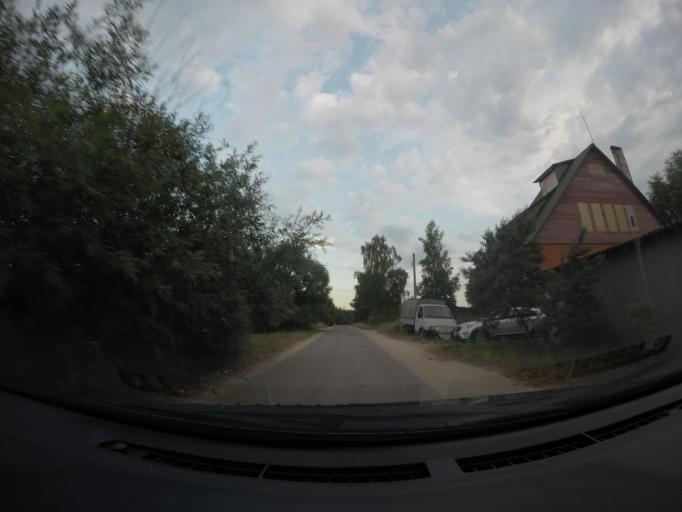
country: RU
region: Moskovskaya
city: Krasnyy Tkach
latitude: 55.3841
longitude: 39.2037
